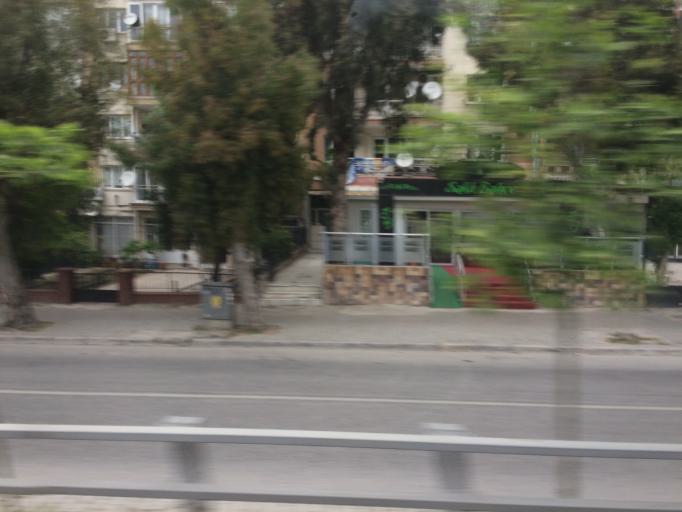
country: TR
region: Izmir
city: Bornova
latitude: 38.4570
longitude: 27.2038
